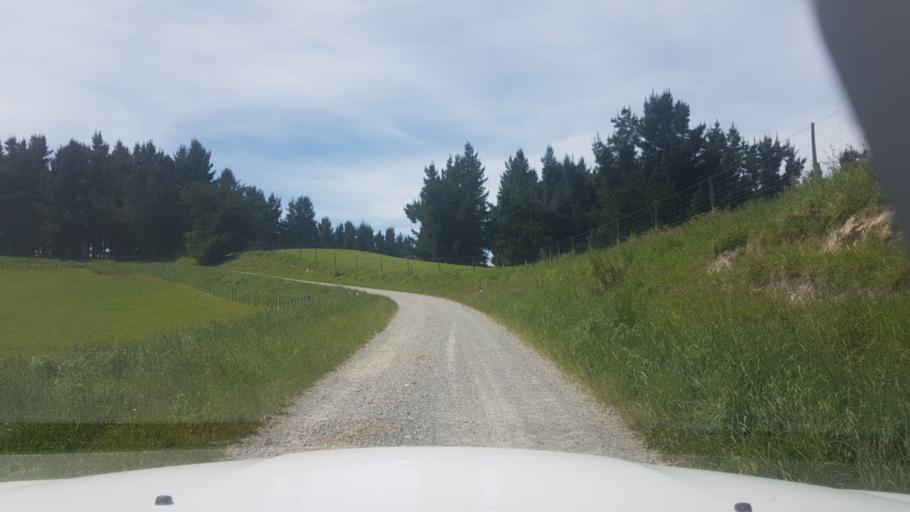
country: NZ
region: Canterbury
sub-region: Timaru District
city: Pleasant Point
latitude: -44.1483
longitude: 171.0210
